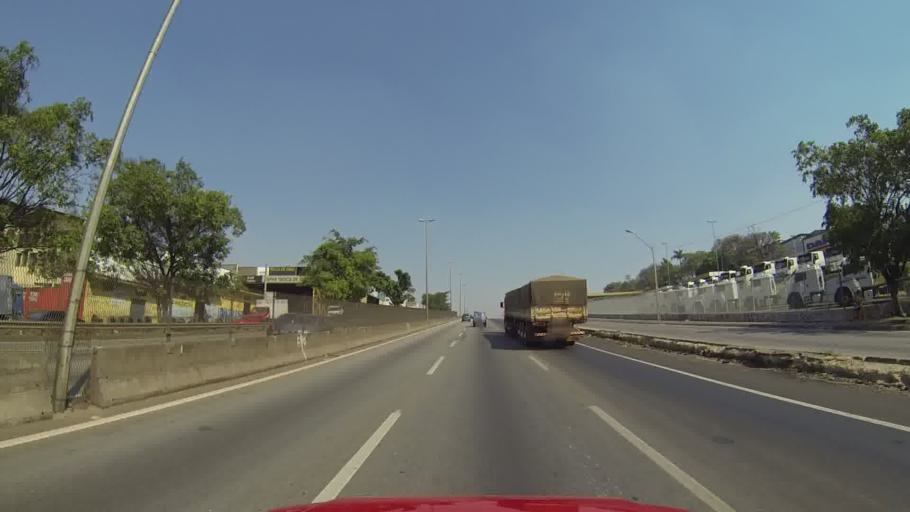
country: BR
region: Minas Gerais
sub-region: Contagem
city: Contagem
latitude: -19.9625
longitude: -44.0496
